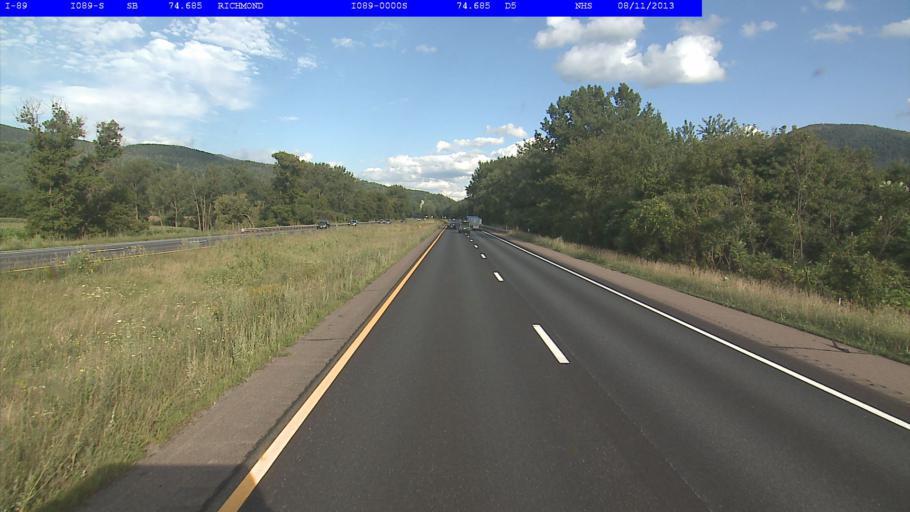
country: US
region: Vermont
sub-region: Chittenden County
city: Jericho
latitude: 44.3916
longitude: -72.9562
